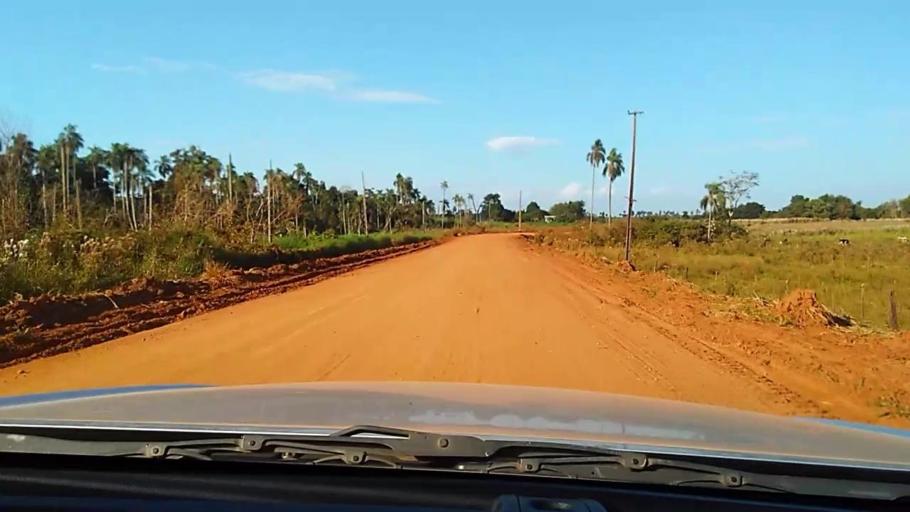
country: PY
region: Alto Parana
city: Santa Rita
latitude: -25.7047
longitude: -55.3823
